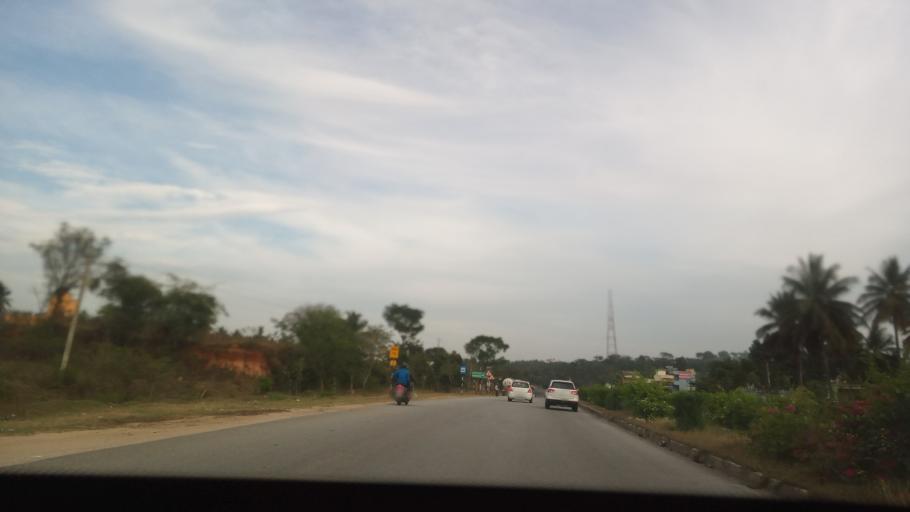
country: IN
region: Karnataka
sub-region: Ramanagara
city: Magadi
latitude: 13.0762
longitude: 77.2079
